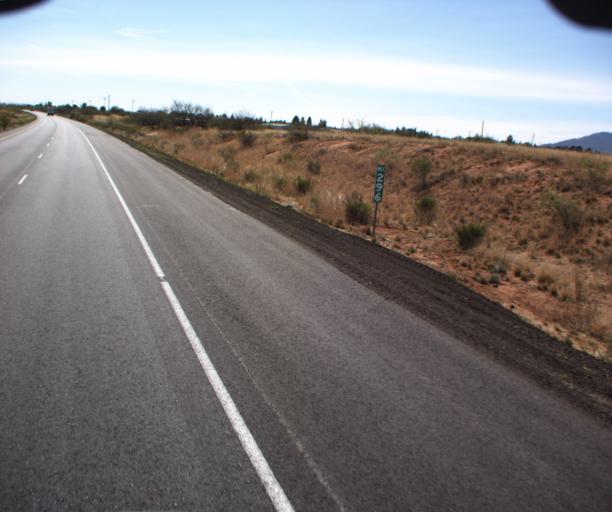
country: US
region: Arizona
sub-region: Cochise County
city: Mescal
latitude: 31.9637
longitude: -110.4548
